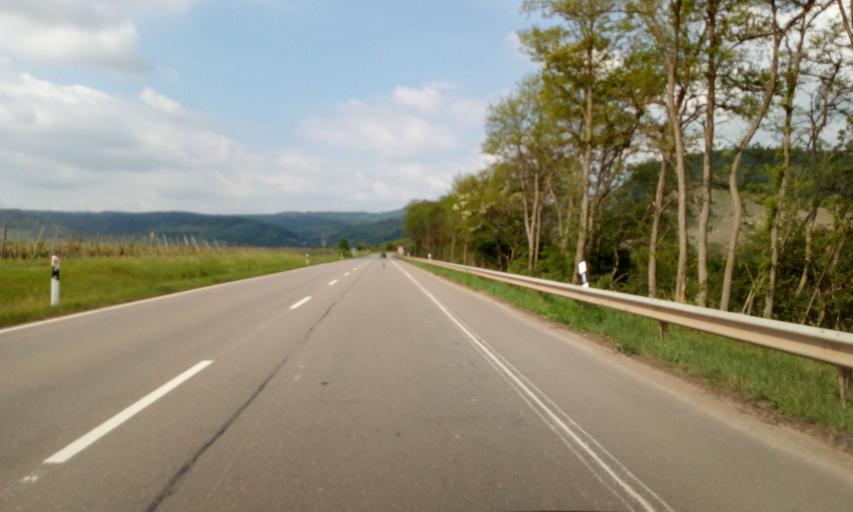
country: DE
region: Rheinland-Pfalz
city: Klusserath
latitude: 49.8401
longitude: 6.8559
